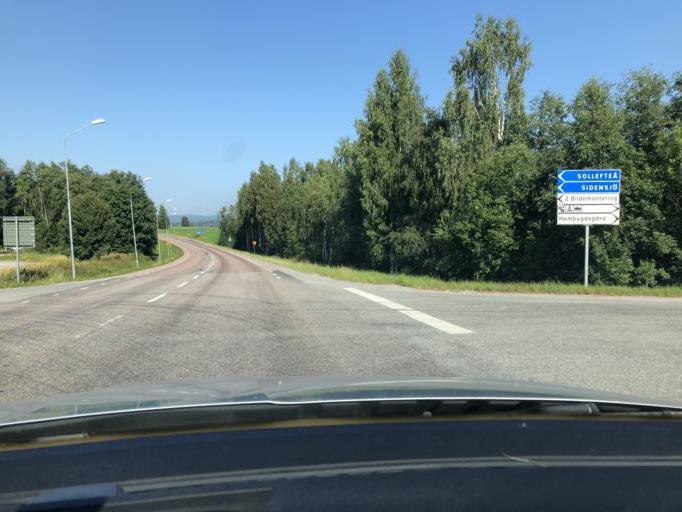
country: SE
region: Vaesternorrland
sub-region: OErnskoeldsviks Kommun
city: Bjasta
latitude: 63.2863
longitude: 18.5669
